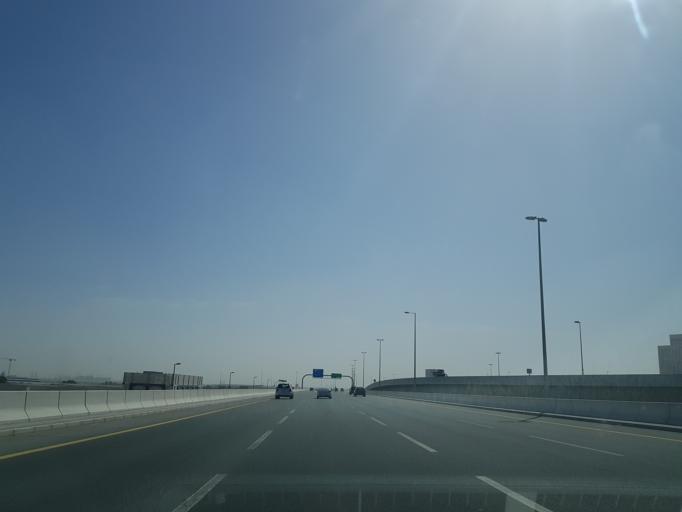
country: AE
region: Dubai
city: Dubai
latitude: 24.9904
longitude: 55.0941
